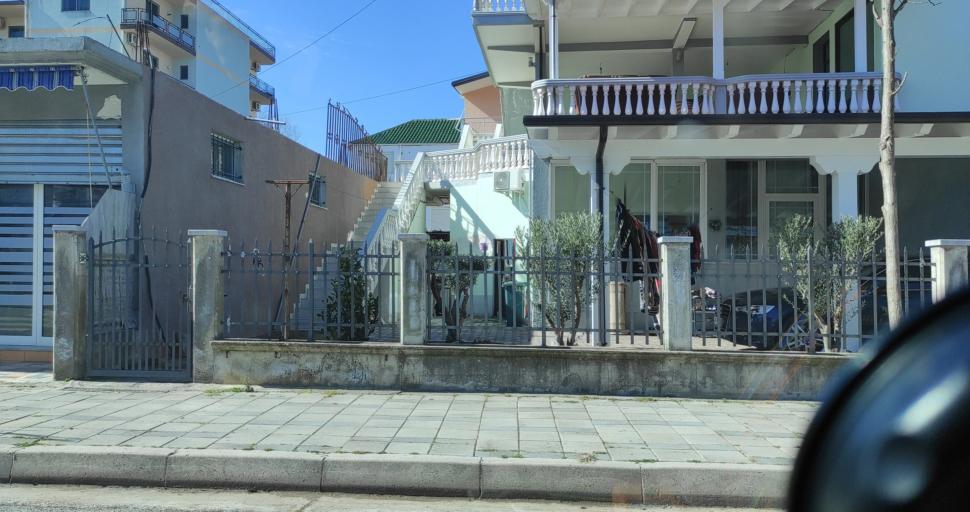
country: AL
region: Shkoder
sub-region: Rrethi i Shkodres
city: Velipoje
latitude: 41.8656
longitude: 19.4261
